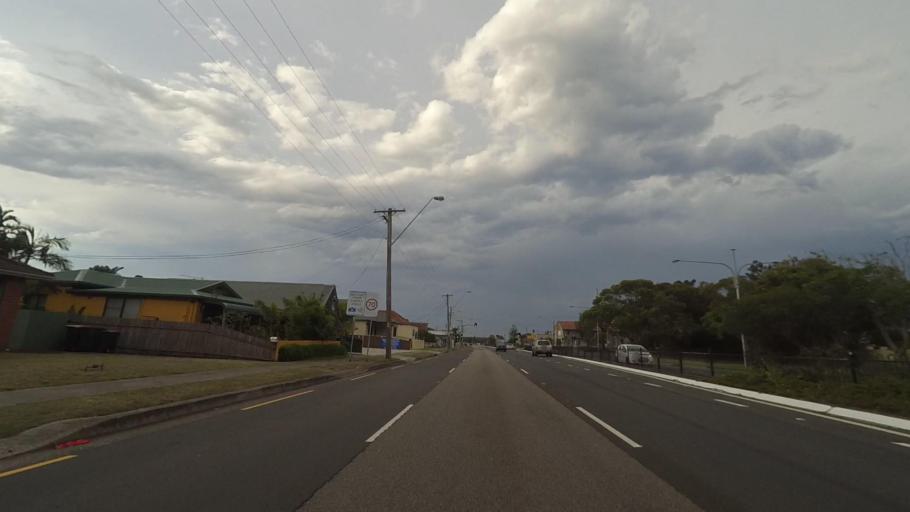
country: AU
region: New South Wales
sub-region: Shellharbour
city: Lake Illawarra
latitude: -34.5314
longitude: 150.8688
